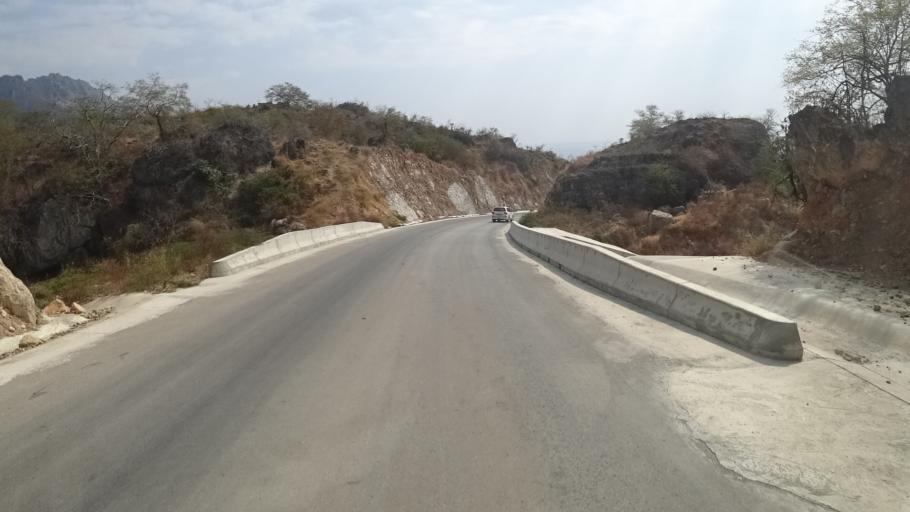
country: YE
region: Al Mahrah
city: Hawf
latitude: 16.7100
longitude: 53.2580
